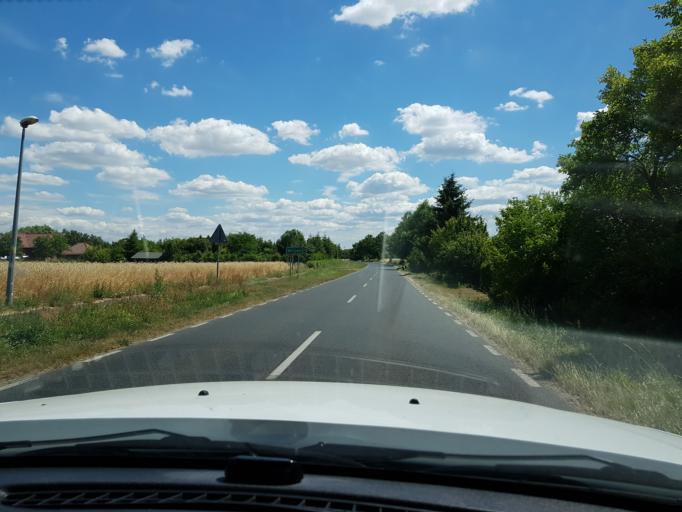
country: PL
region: West Pomeranian Voivodeship
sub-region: Powiat mysliborski
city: Mysliborz
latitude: 52.9216
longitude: 14.8974
